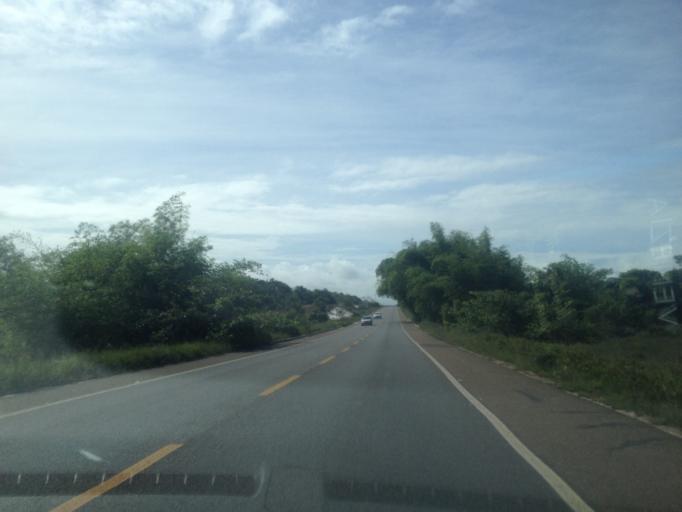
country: BR
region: Bahia
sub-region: Mata De Sao Joao
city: Mata de Sao Joao
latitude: -12.5364
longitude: -37.9976
